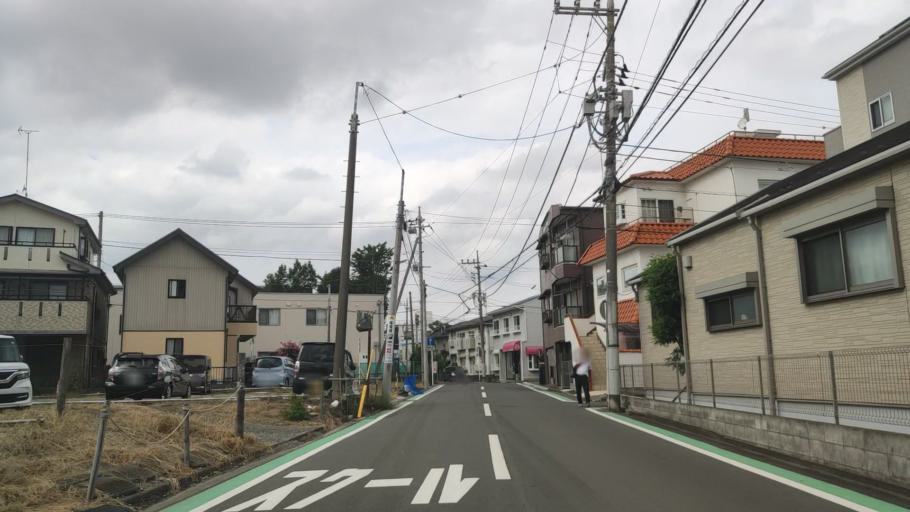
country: JP
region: Kanagawa
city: Minami-rinkan
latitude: 35.4959
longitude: 139.4507
